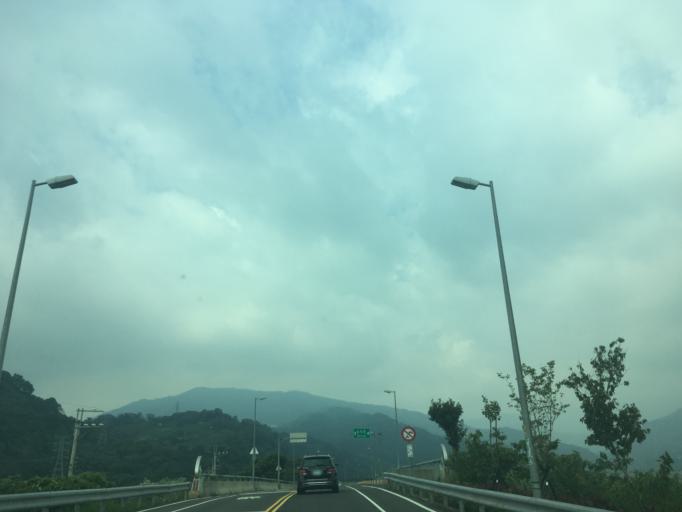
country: TW
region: Taiwan
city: Fengyuan
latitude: 24.2936
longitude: 120.8676
